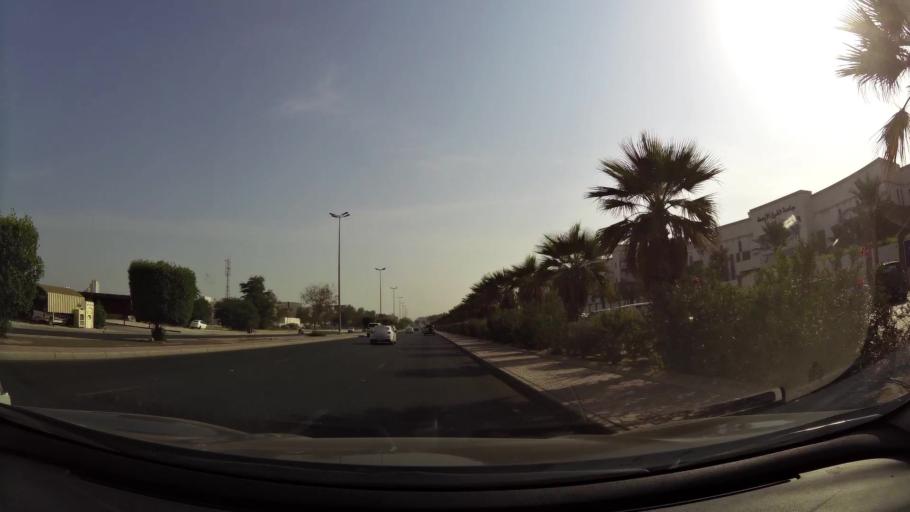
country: KW
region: Al Ahmadi
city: Ar Riqqah
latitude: 29.1653
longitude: 48.1015
